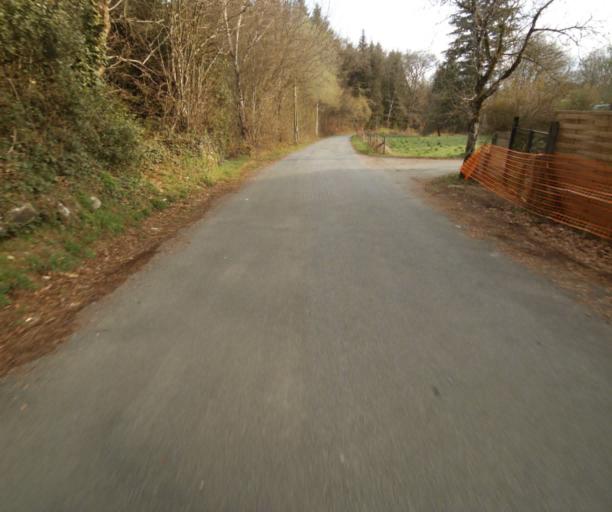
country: FR
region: Limousin
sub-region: Departement de la Correze
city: Correze
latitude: 45.4049
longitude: 1.9012
